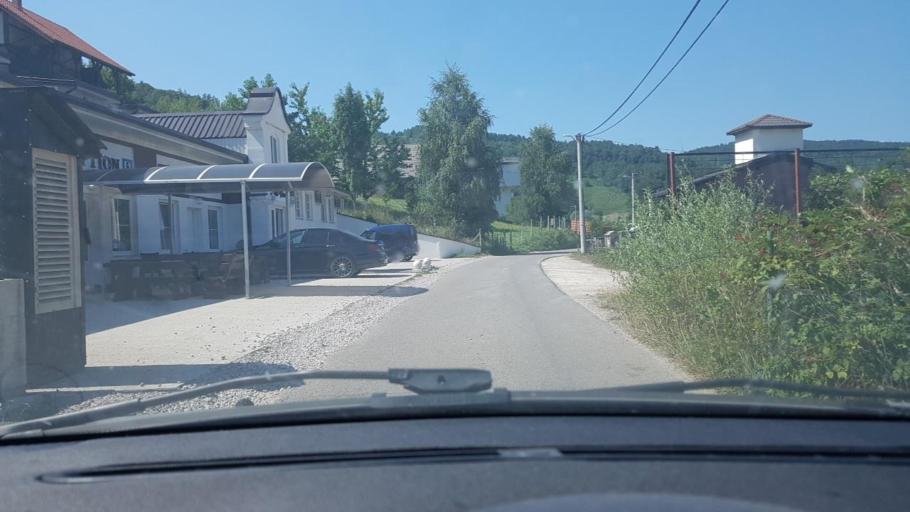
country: BA
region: Federation of Bosnia and Herzegovina
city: Bihac
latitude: 44.7358
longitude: 15.9231
